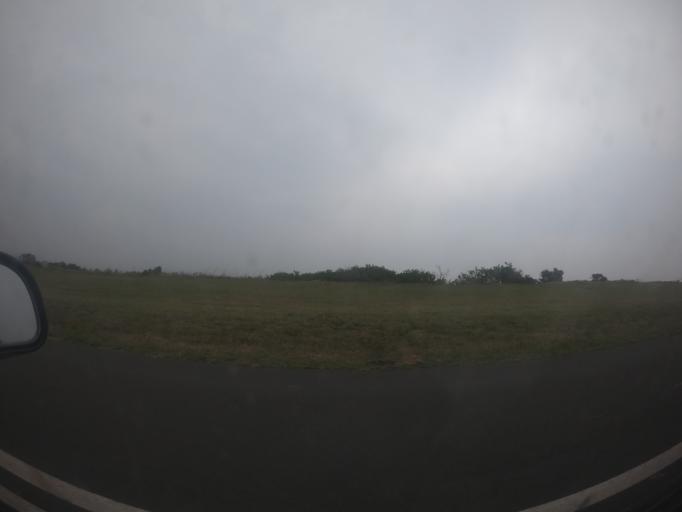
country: AU
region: New South Wales
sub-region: Shellharbour
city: Croom
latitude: -34.6090
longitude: 150.8600
